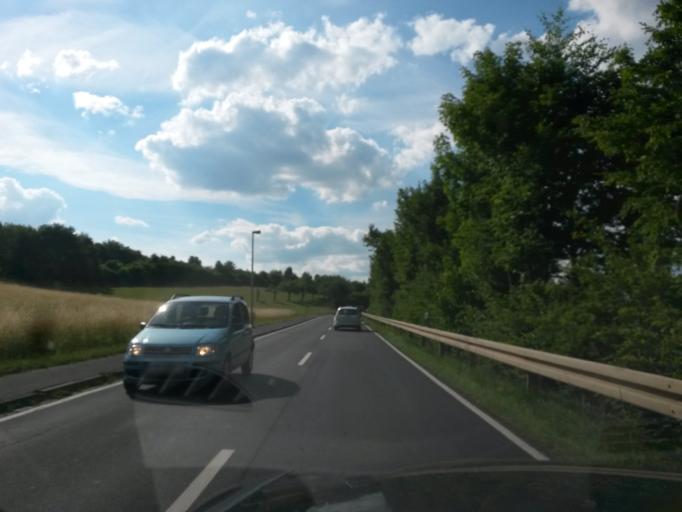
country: DE
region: Bavaria
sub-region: Regierungsbezirk Unterfranken
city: Rimpar
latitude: 49.8478
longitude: 9.9705
